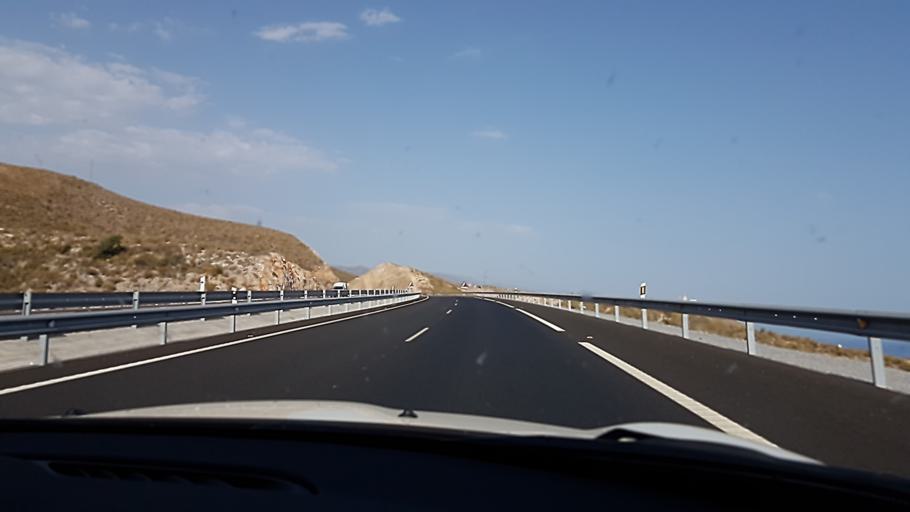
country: ES
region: Andalusia
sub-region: Provincia de Granada
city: Gualchos
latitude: 36.7159
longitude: -3.3830
